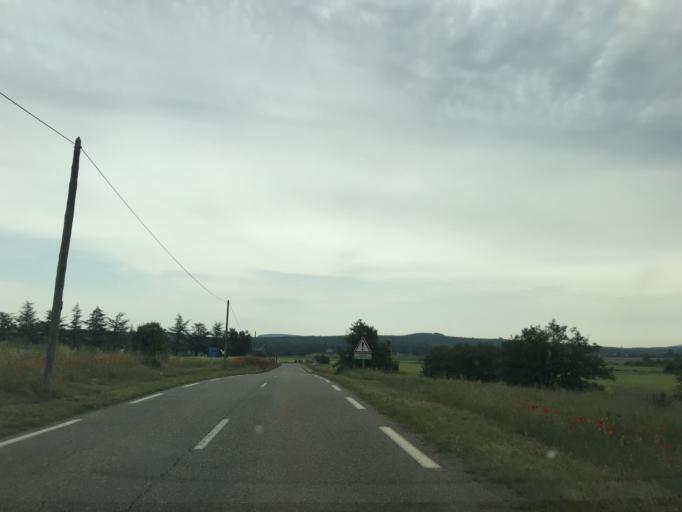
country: FR
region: Provence-Alpes-Cote d'Azur
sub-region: Departement du Var
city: Ginasservis
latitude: 43.6437
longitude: 5.8258
